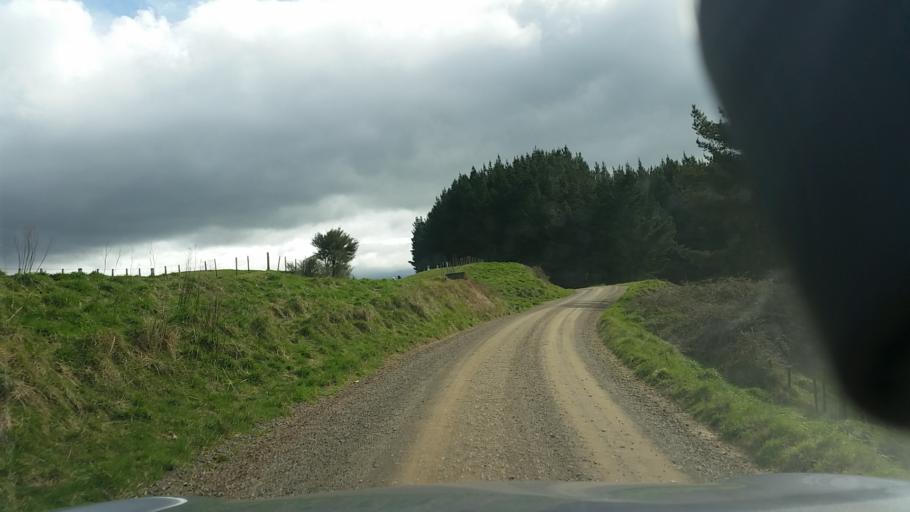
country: NZ
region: Hawke's Bay
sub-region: Napier City
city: Napier
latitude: -39.2052
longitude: 176.9192
